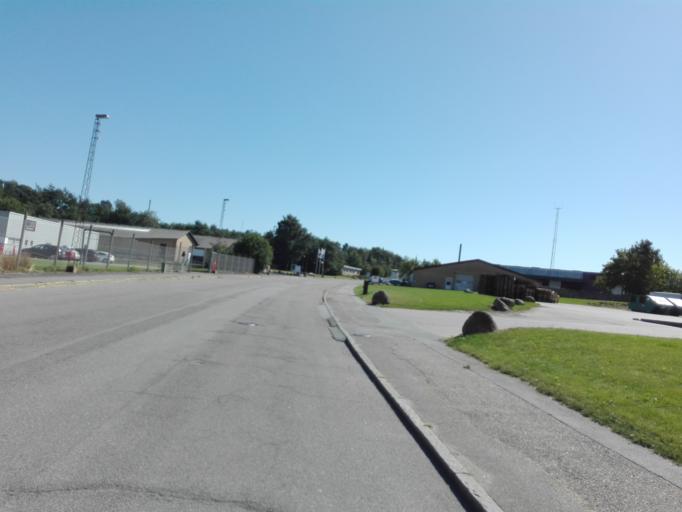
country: DK
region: Central Jutland
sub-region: Arhus Kommune
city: Stavtrup
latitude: 56.1147
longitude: 10.1411
